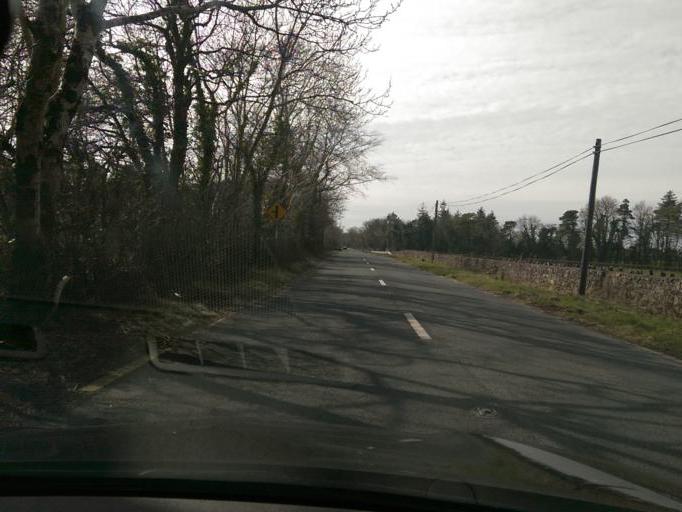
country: IE
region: Connaught
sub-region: County Galway
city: Athenry
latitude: 53.4475
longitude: -8.7113
